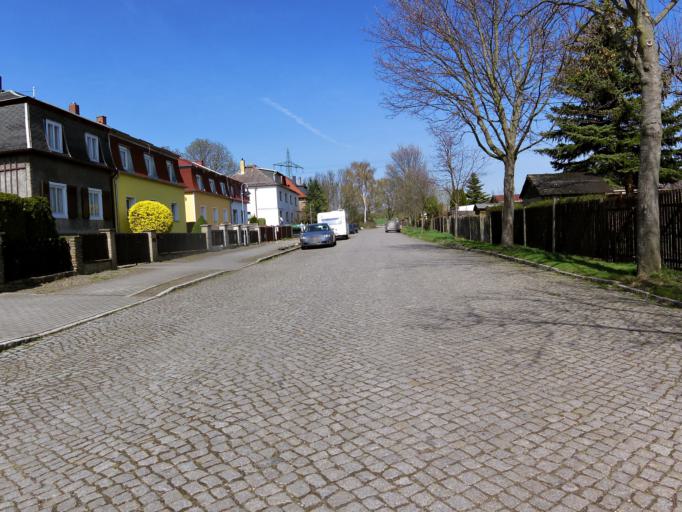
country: DE
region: Saxony
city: Schkeuditz
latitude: 51.3892
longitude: 12.2832
